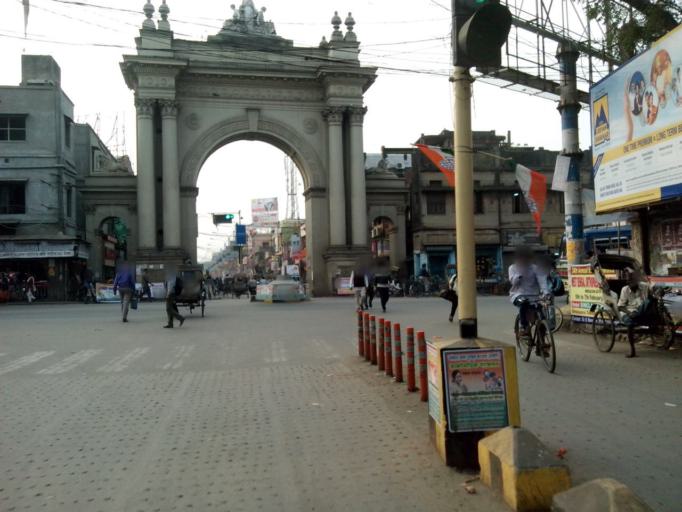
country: IN
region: West Bengal
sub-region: Barddhaman
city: Barddhaman
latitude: 23.2368
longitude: 87.8664
